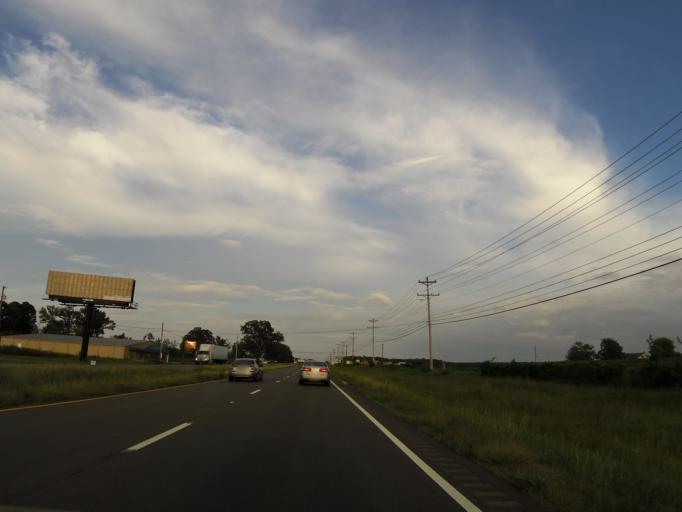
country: US
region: Alabama
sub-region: Madison County
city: Madison
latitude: 34.7629
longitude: -86.8530
